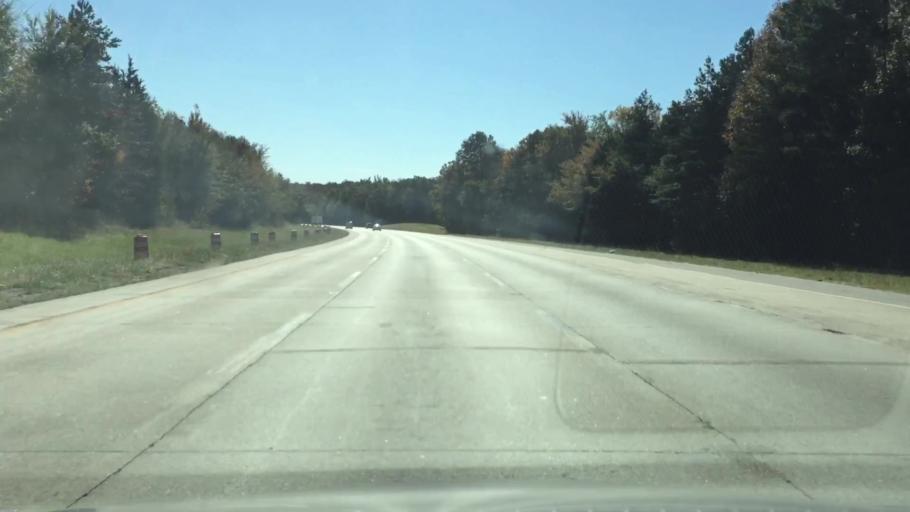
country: US
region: North Carolina
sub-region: Guilford County
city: Jamestown
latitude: 35.9811
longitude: -79.8886
